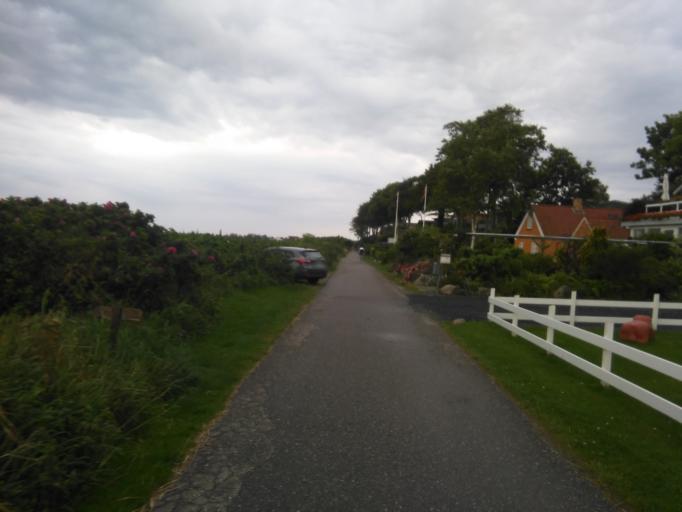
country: DK
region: Central Jutland
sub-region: Arhus Kommune
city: Logten
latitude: 56.2286
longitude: 10.3131
